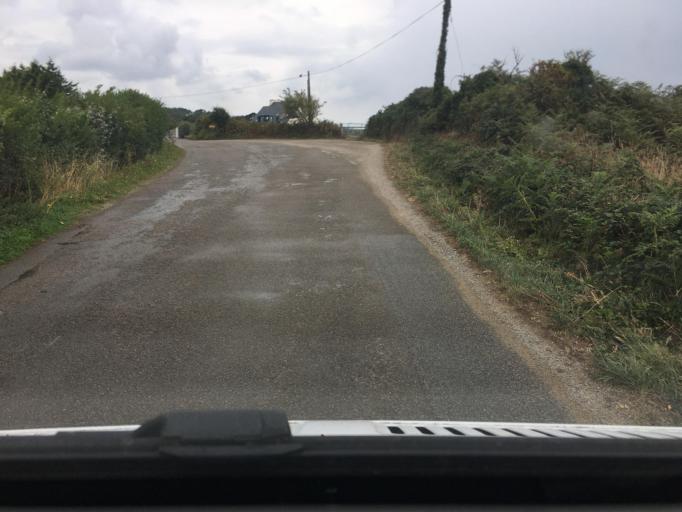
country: FR
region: Brittany
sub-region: Departement du Finistere
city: Beuzec-Cap-Sizun
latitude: 48.0843
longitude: -4.4806
